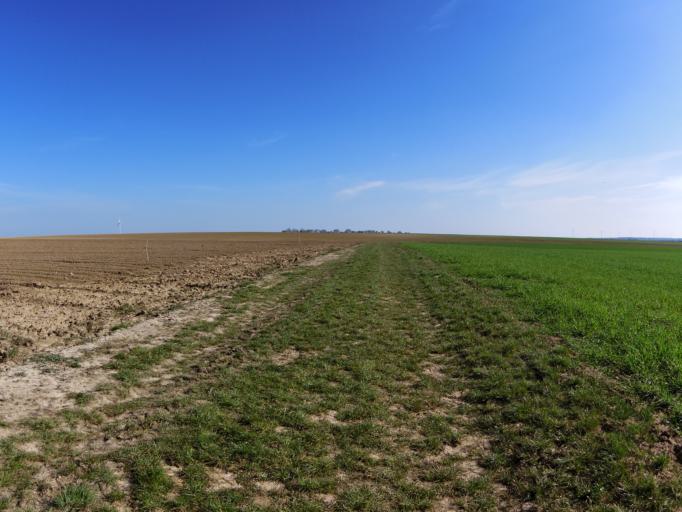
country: DE
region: Bavaria
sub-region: Regierungsbezirk Unterfranken
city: Prosselsheim
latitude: 49.8491
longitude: 10.1113
